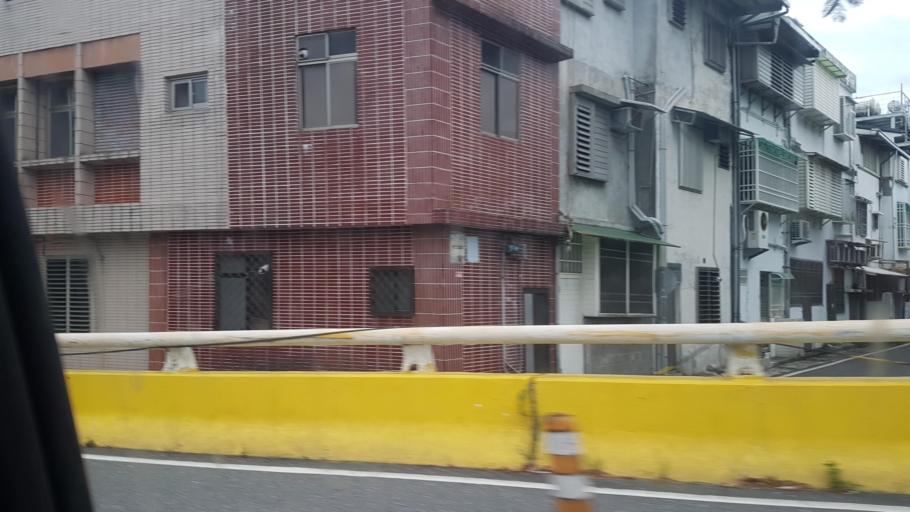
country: TW
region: Taiwan
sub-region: Hualien
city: Hualian
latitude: 23.9802
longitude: 121.5970
